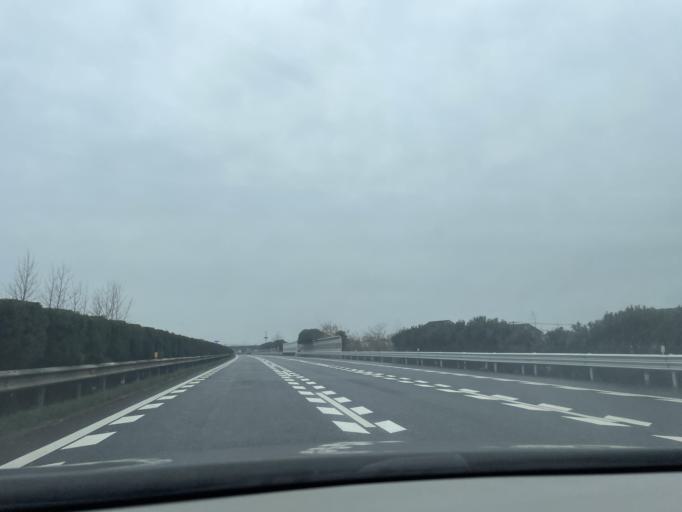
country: CN
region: Zhejiang Sheng
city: Liutangting
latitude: 30.2865
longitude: 121.2589
